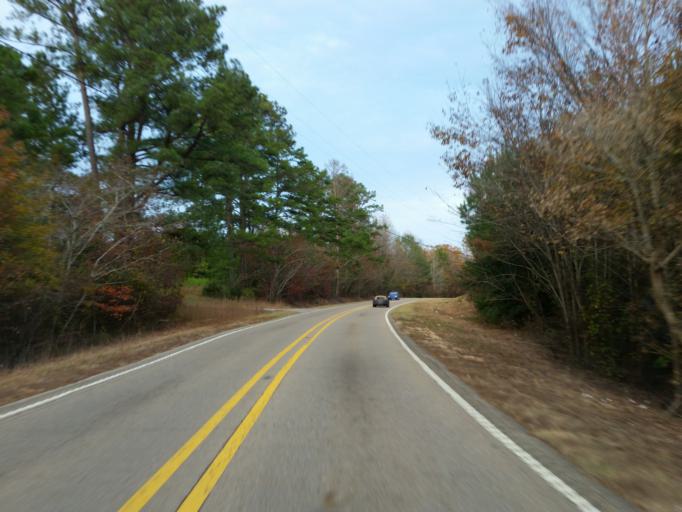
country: US
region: Mississippi
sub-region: Lauderdale County
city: Marion
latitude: 32.4183
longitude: -88.5381
